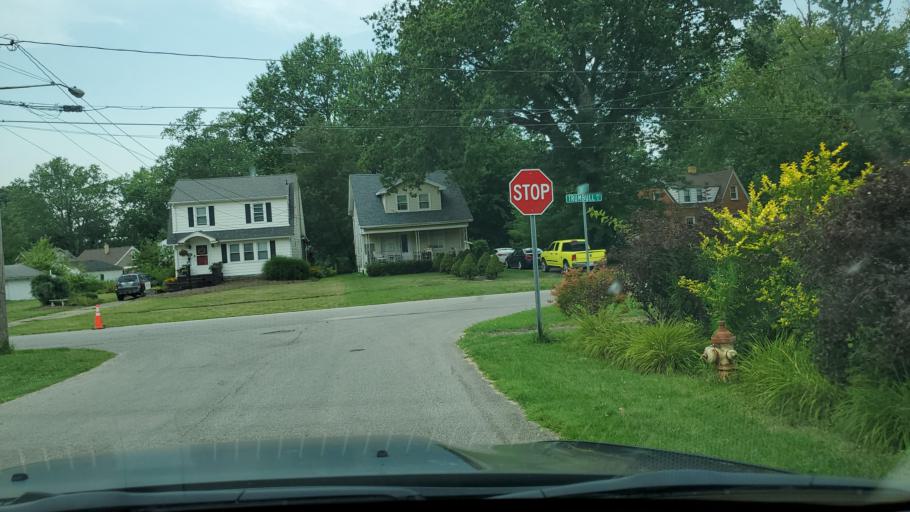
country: US
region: Ohio
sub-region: Trumbull County
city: Bolindale
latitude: 41.2249
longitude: -80.7811
